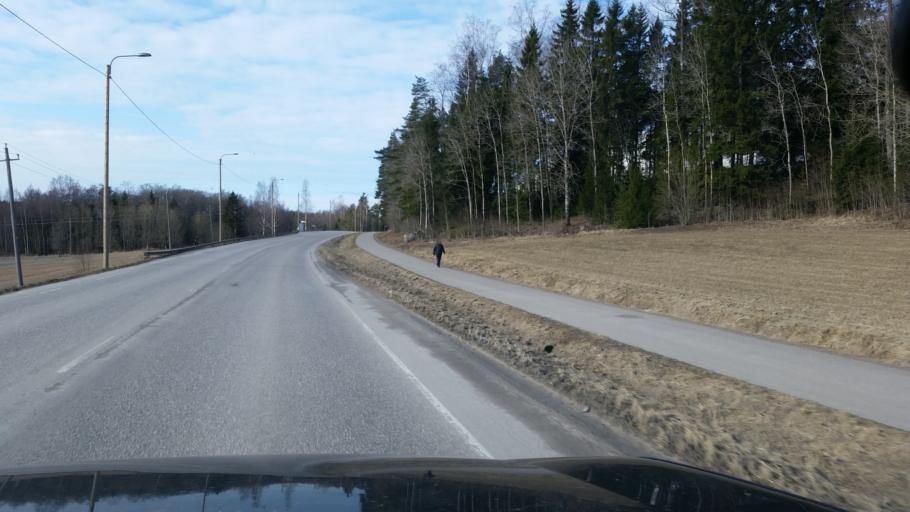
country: FI
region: Uusimaa
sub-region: Helsinki
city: Kirkkonummi
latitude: 60.1044
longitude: 24.4351
